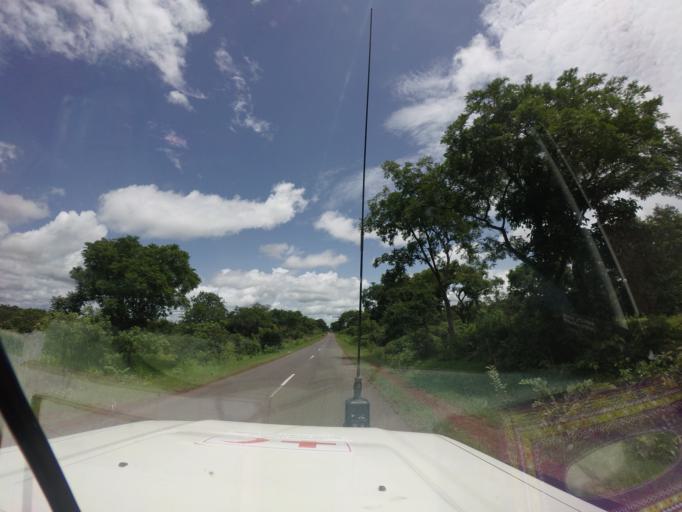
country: SL
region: Northern Province
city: Gberia Fotombu
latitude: 10.0559
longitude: -11.0642
